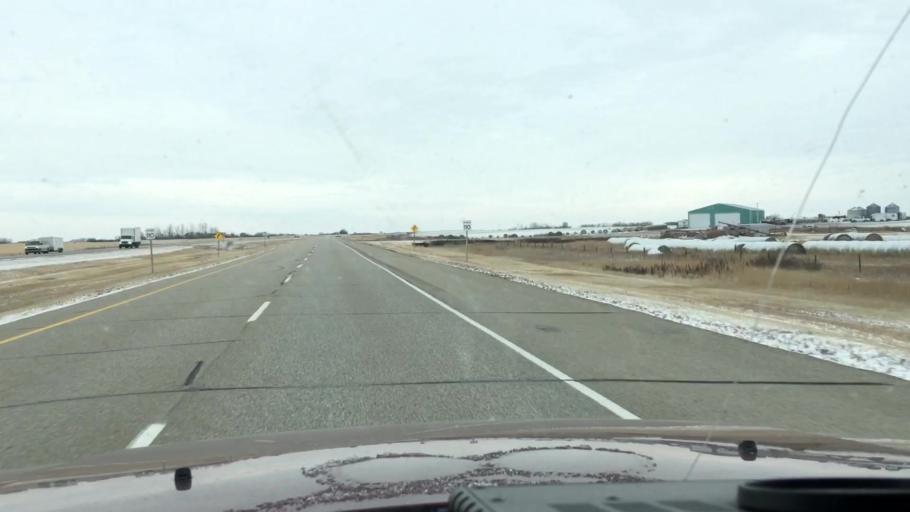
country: CA
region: Saskatchewan
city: Watrous
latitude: 51.3668
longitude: -106.1328
